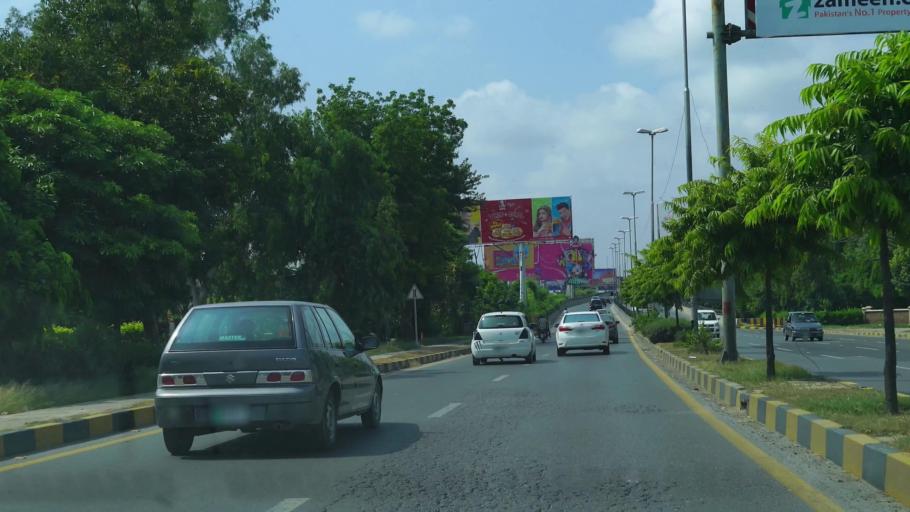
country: PK
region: Punjab
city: Lahore
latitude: 31.5273
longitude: 74.3619
